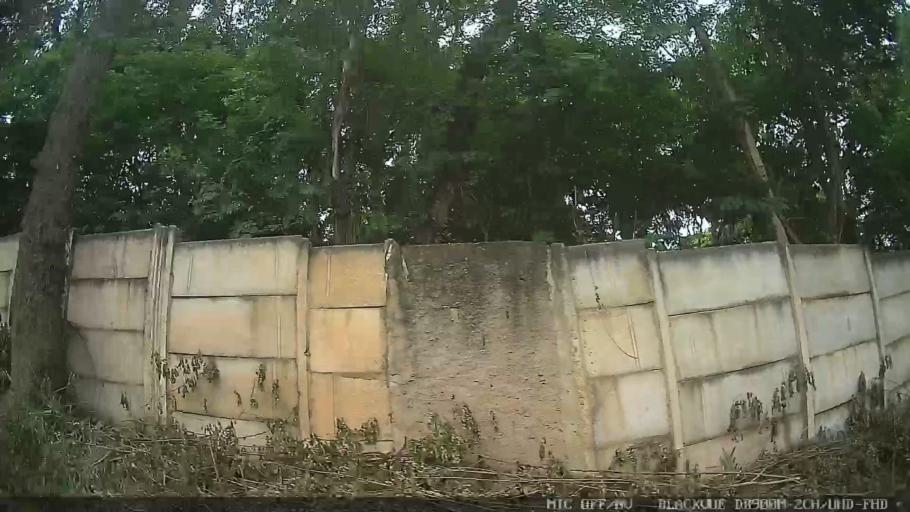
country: BR
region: Sao Paulo
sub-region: Santa Isabel
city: Santa Isabel
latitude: -23.3387
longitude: -46.2161
